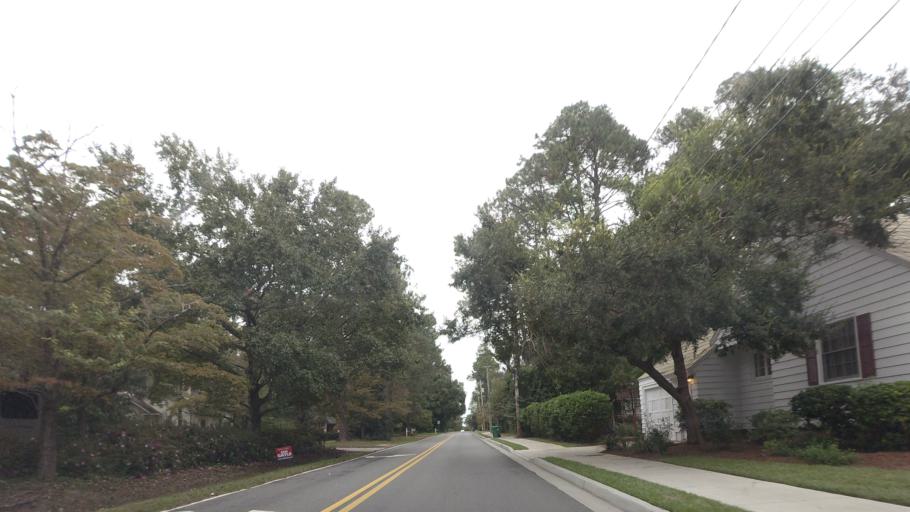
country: US
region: Georgia
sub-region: Lowndes County
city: Remerton
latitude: 30.8524
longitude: -83.2928
